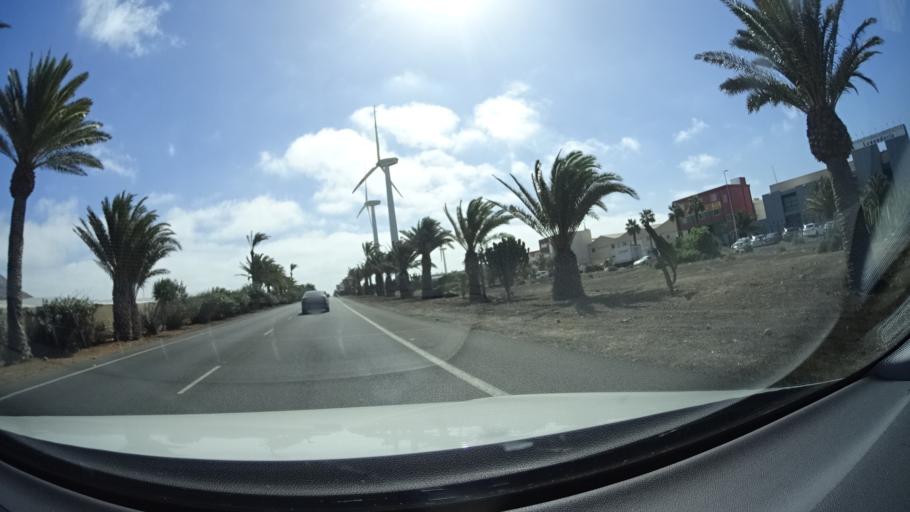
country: ES
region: Canary Islands
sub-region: Provincia de Las Palmas
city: Cruce de Arinaga
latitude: 27.8644
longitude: -15.4083
